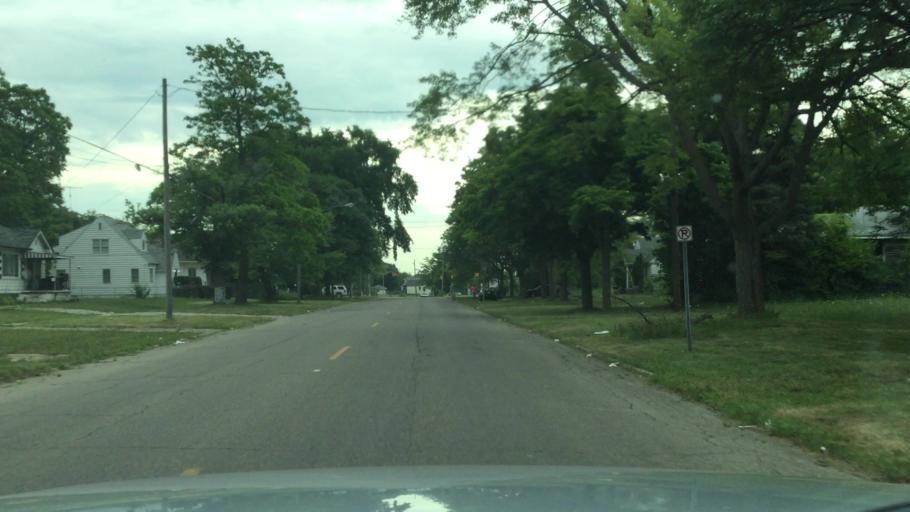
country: US
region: Michigan
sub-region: Genesee County
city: Beecher
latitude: 43.0560
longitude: -83.6967
